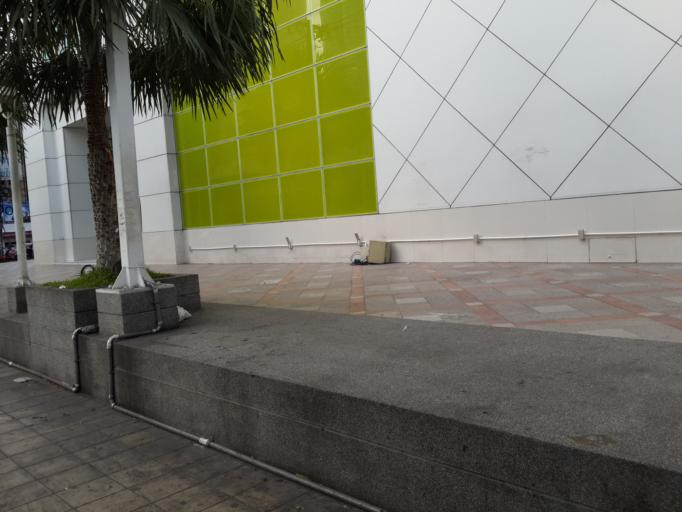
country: TH
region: Bangkok
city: Ratchathewi
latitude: 13.7501
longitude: 100.5418
